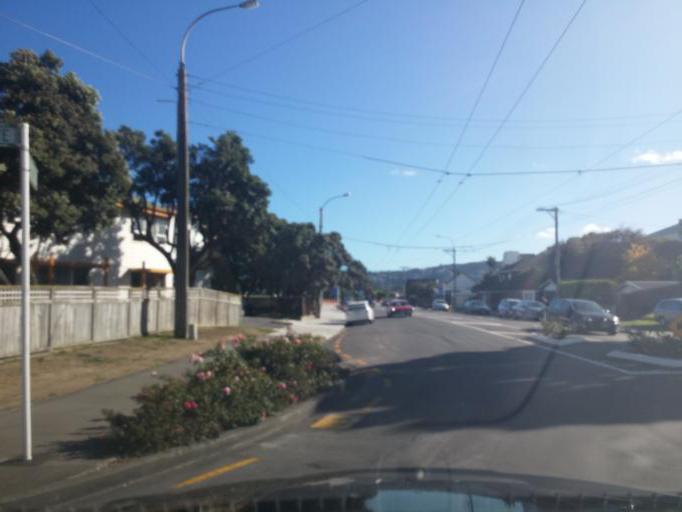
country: NZ
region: Wellington
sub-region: Wellington City
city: Wellington
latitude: -41.3246
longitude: 174.8203
